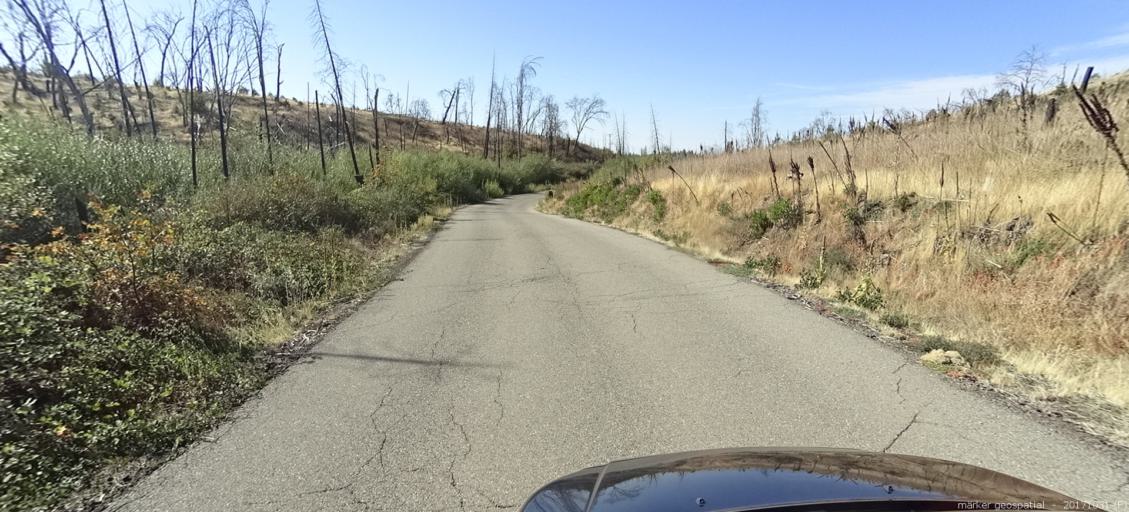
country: US
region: California
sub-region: Shasta County
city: Shingletown
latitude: 40.4537
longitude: -121.7985
